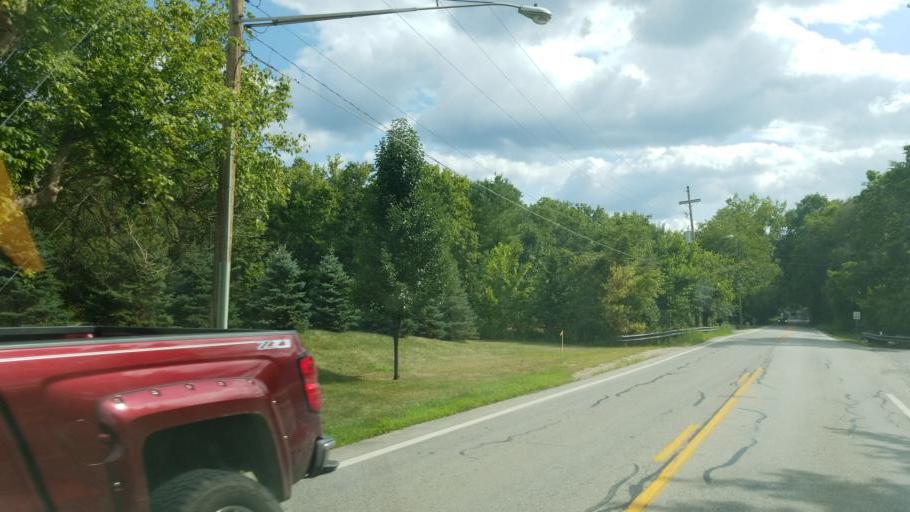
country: US
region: Ohio
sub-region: Delaware County
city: Powell
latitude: 40.1640
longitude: -83.0449
